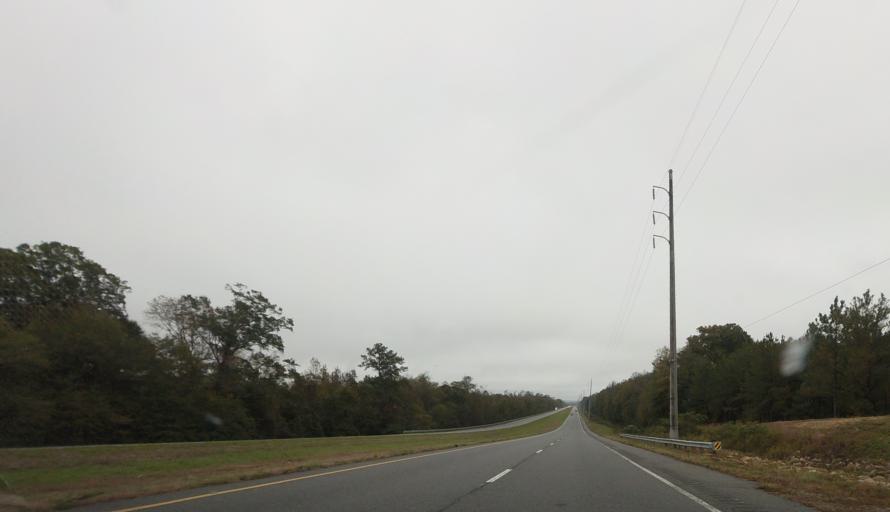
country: US
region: Georgia
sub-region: Taylor County
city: Reynolds
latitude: 32.5541
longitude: -84.0568
